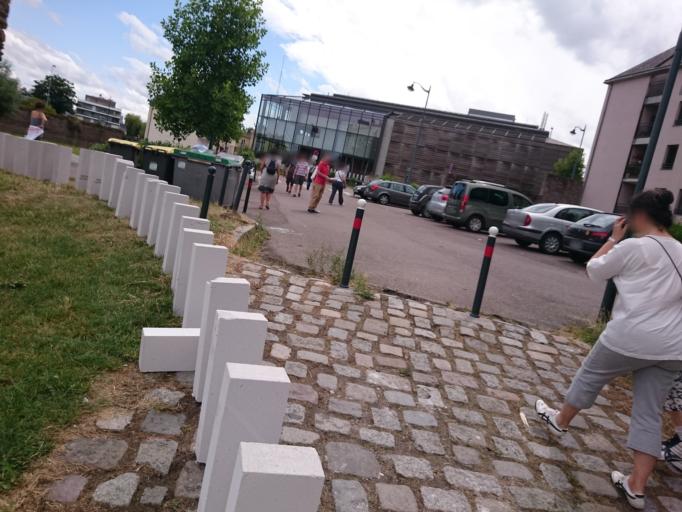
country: FR
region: Brittany
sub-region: Departement d'Ille-et-Vilaine
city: Rennes
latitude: 48.1099
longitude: -1.6968
